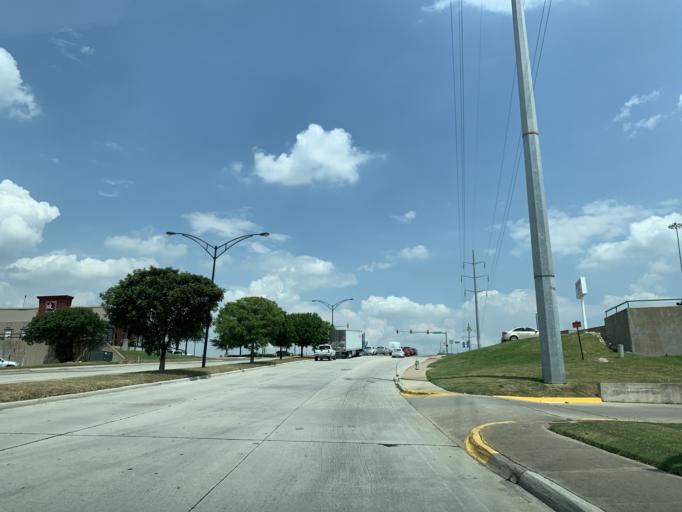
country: US
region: Texas
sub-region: Tarrant County
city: Richland Hills
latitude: 32.7662
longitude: -97.2149
